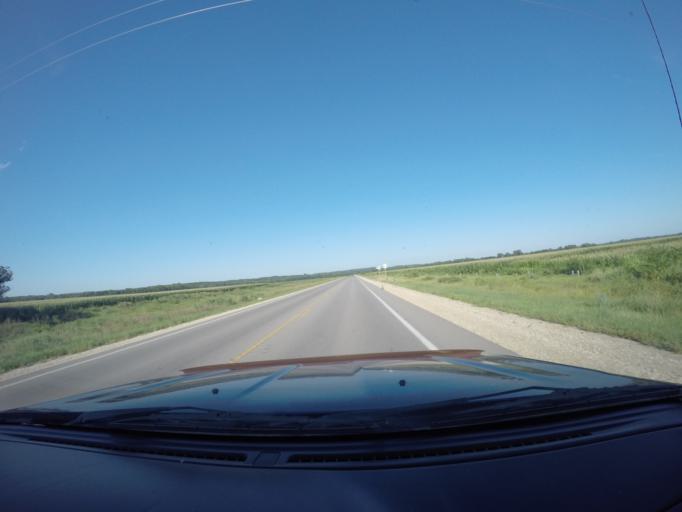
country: US
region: Kansas
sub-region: Jefferson County
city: Oskaloosa
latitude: 39.0873
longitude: -95.4256
